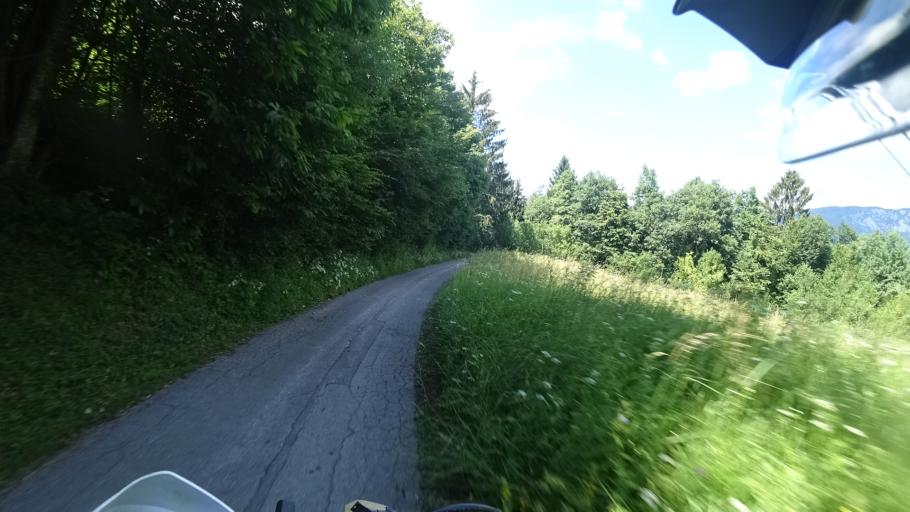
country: SI
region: Osilnica
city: Osilnica
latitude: 45.5151
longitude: 14.6919
